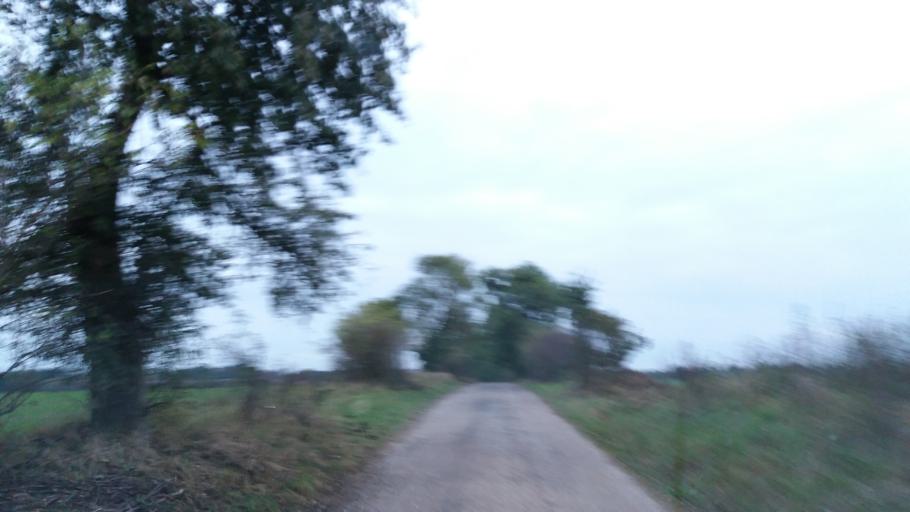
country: PL
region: West Pomeranian Voivodeship
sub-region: Powiat choszczenski
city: Choszczno
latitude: 53.0970
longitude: 15.4054
